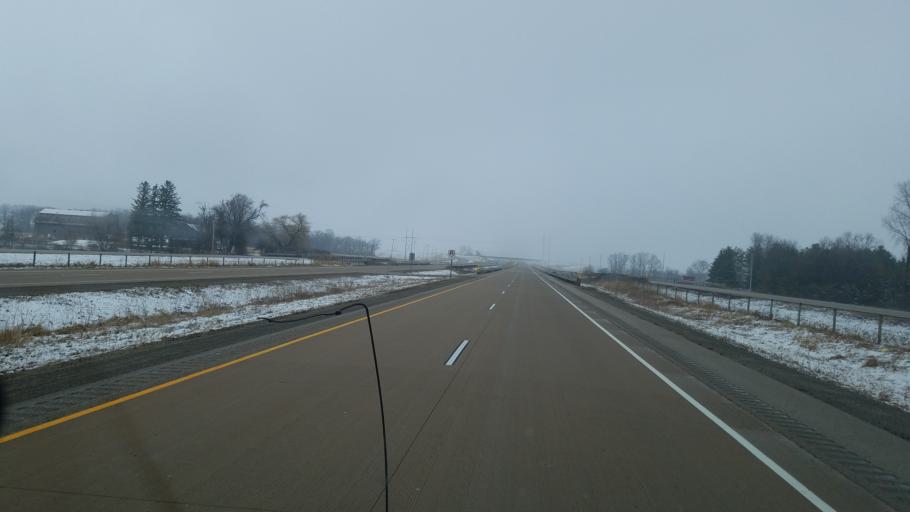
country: US
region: Wisconsin
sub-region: Winnebago County
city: Winneconne
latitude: 44.1617
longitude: -88.6642
